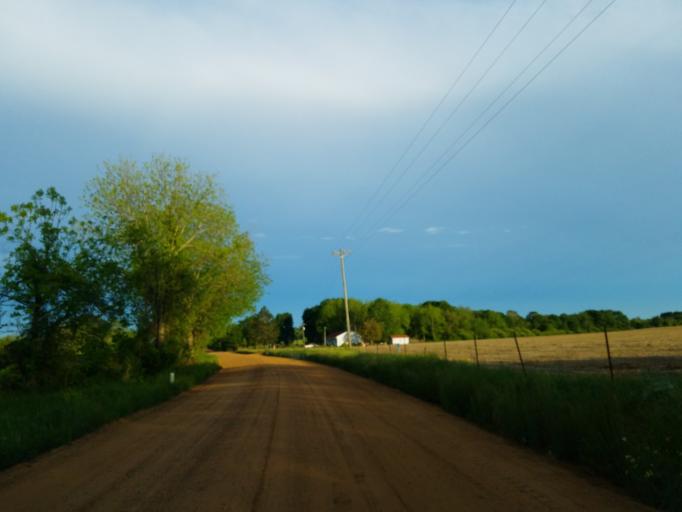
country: US
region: Georgia
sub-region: Turner County
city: Ashburn
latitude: 31.6509
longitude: -83.6282
